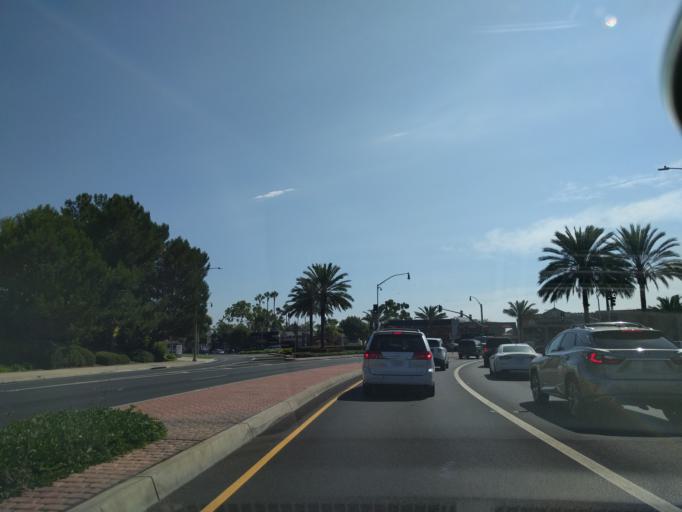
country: US
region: California
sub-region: Orange County
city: San Joaquin Hills
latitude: 33.6048
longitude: -117.8735
